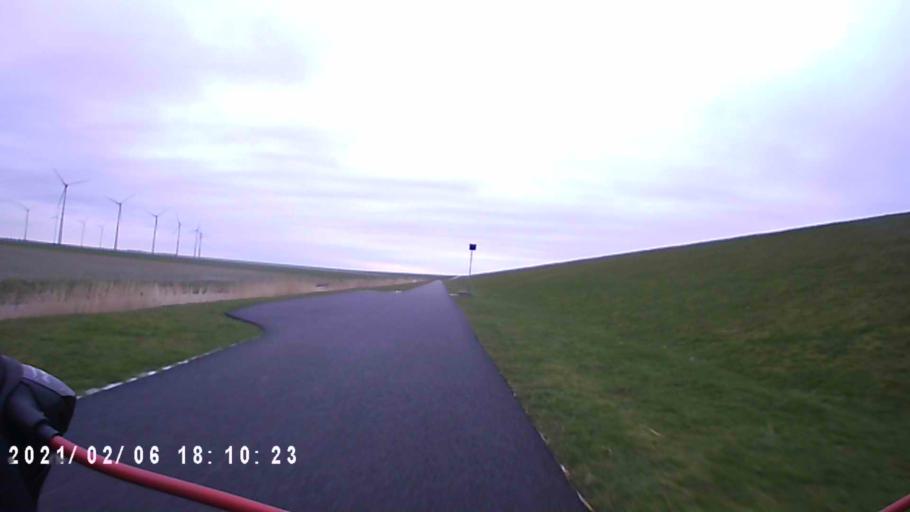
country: NL
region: Groningen
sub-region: Gemeente Appingedam
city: Appingedam
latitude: 53.4569
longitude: 6.7880
